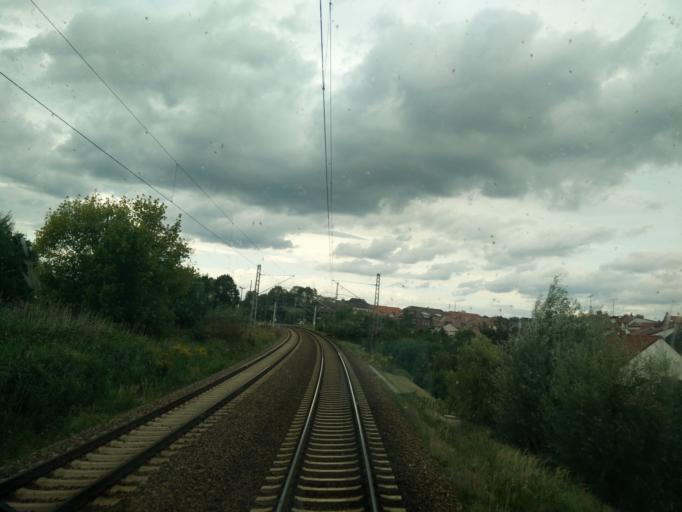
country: DE
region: Brandenburg
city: Luebben
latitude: 51.9321
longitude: 13.8880
